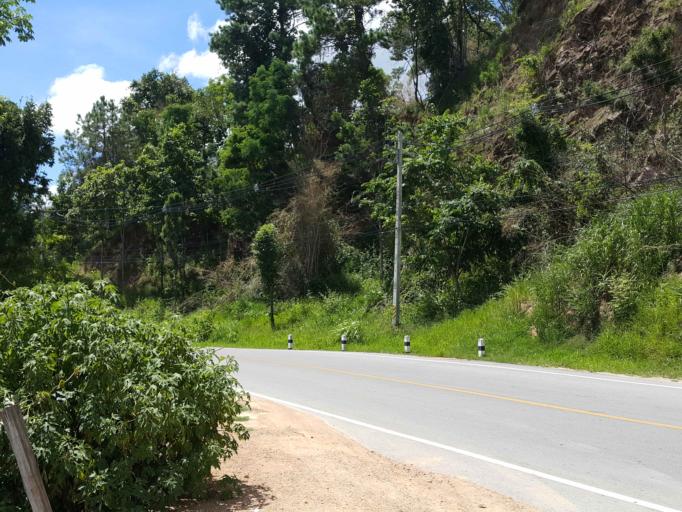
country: TH
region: Chiang Mai
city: Samoeng
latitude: 18.8727
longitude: 98.7817
